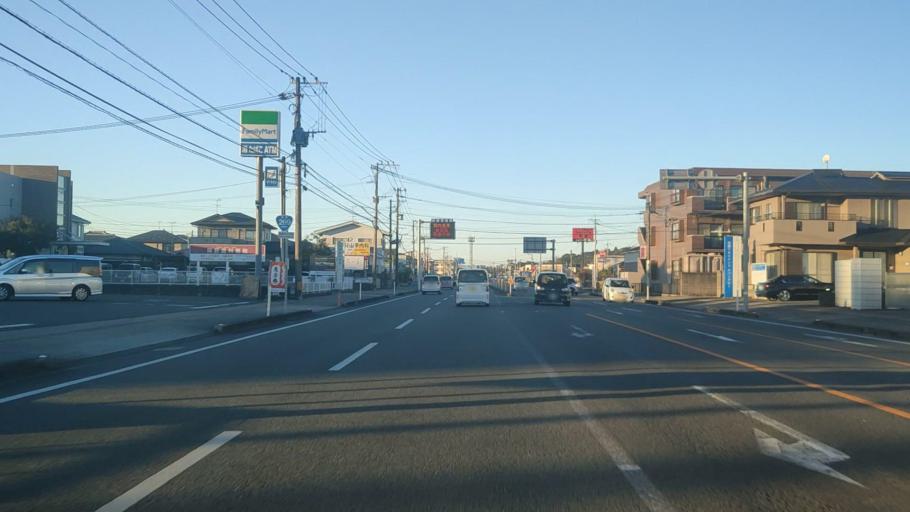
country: JP
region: Miyazaki
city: Miyazaki-shi
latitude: 31.8962
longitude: 131.4067
